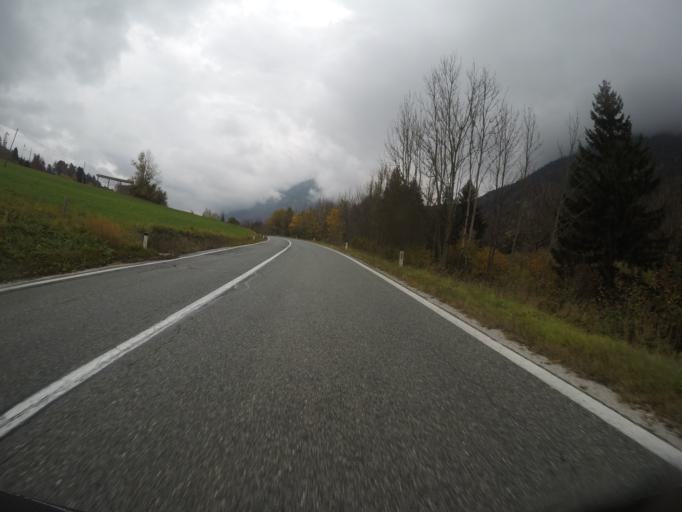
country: SI
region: Kranjska Gora
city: Mojstrana
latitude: 46.4688
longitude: 13.9230
